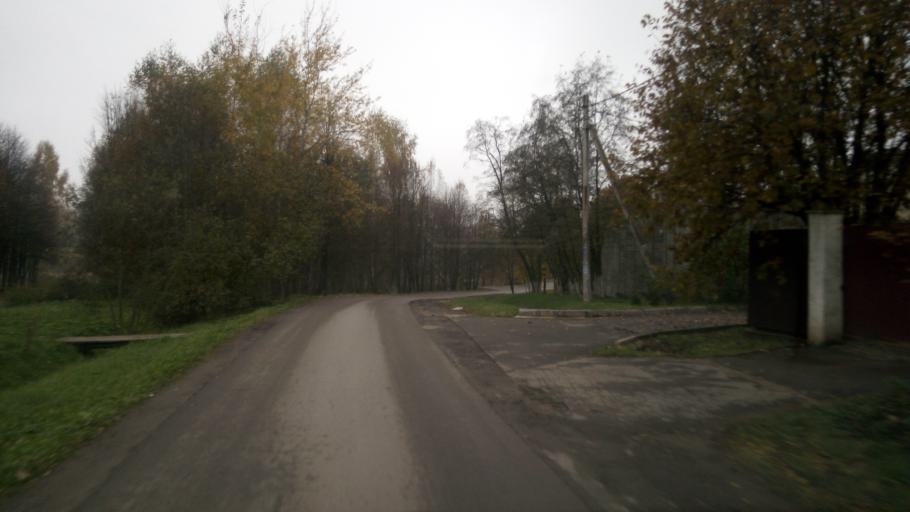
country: RU
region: Moskovskaya
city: Skhodnya
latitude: 55.9339
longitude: 37.2798
